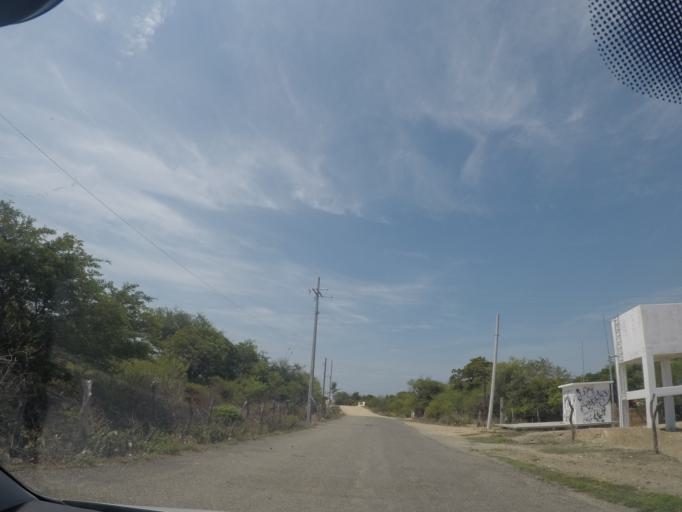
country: MX
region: Oaxaca
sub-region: Salina Cruz
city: Salina Cruz
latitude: 16.1929
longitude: -95.1192
